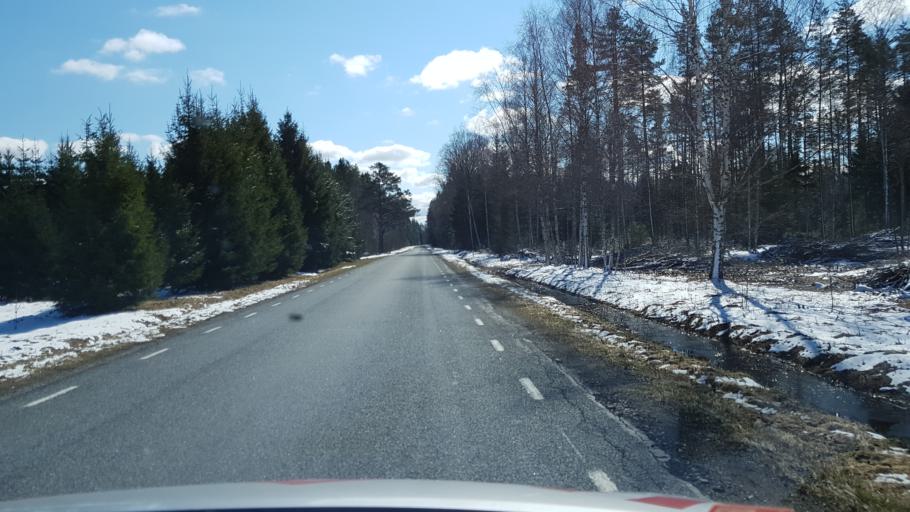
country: EE
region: Laeaene-Virumaa
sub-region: Kadrina vald
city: Kadrina
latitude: 59.4916
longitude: 25.9838
